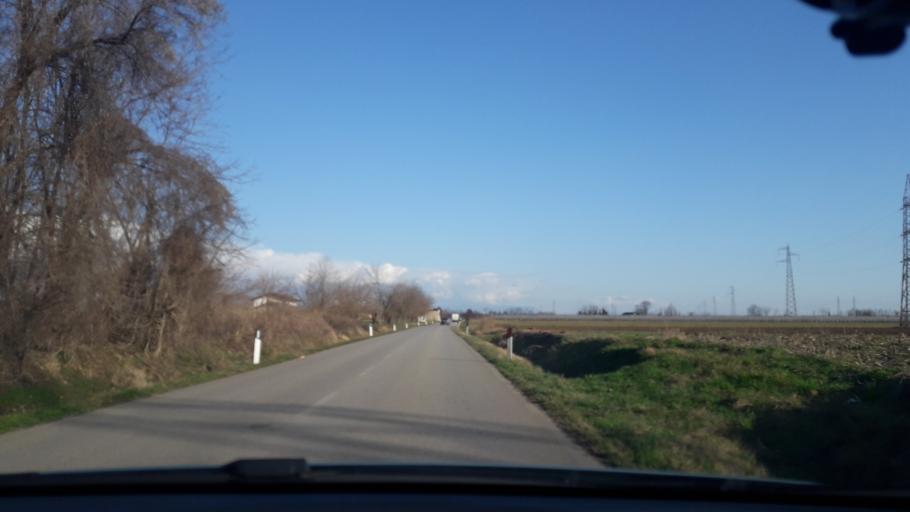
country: IT
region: Friuli Venezia Giulia
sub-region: Provincia di Udine
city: Martignacco
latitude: 46.0760
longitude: 13.1532
